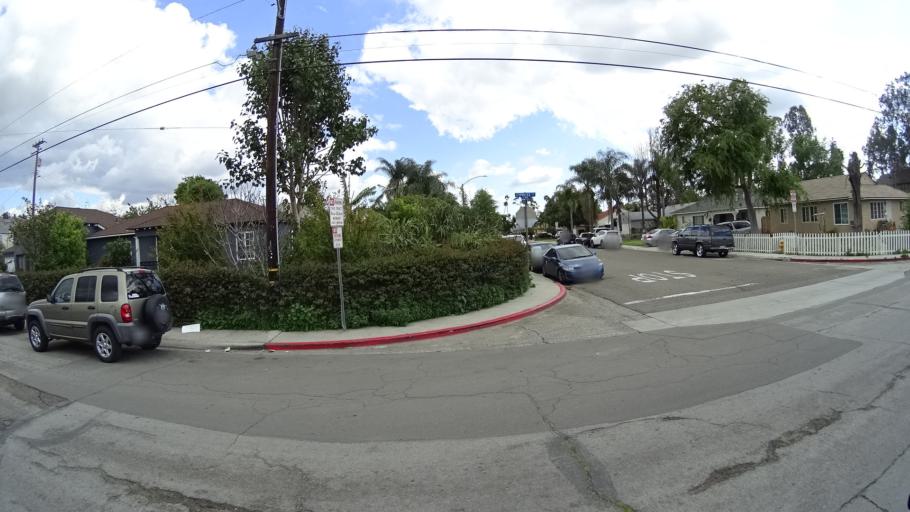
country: US
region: California
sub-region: Orange County
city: Anaheim
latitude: 33.8397
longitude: -117.9057
